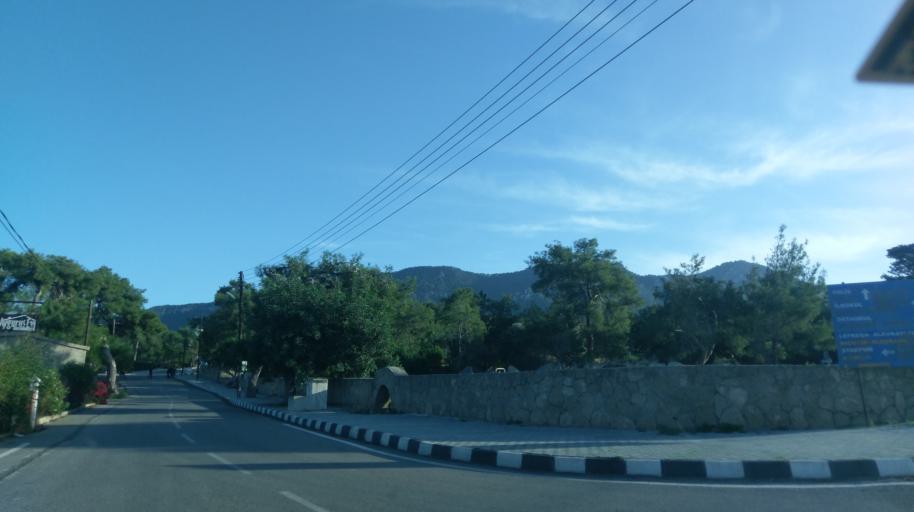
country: CY
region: Ammochostos
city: Lefkonoiko
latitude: 35.3355
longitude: 33.5841
